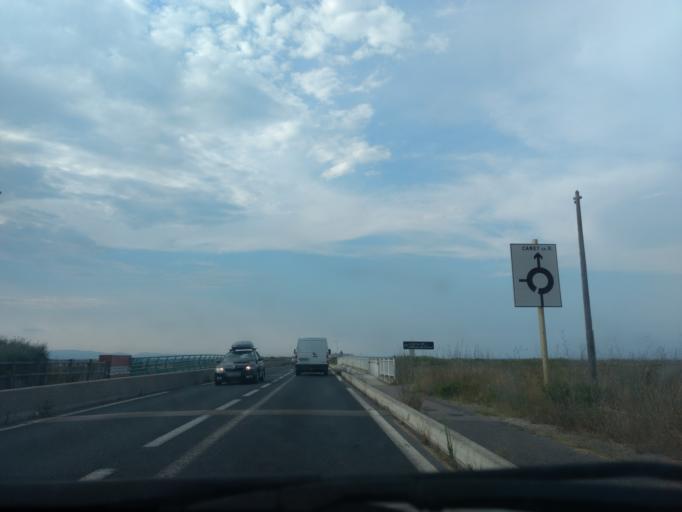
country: FR
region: Languedoc-Roussillon
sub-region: Departement des Pyrenees-Orientales
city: Saint-Cyprien-Plage
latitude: 42.6567
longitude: 3.0329
